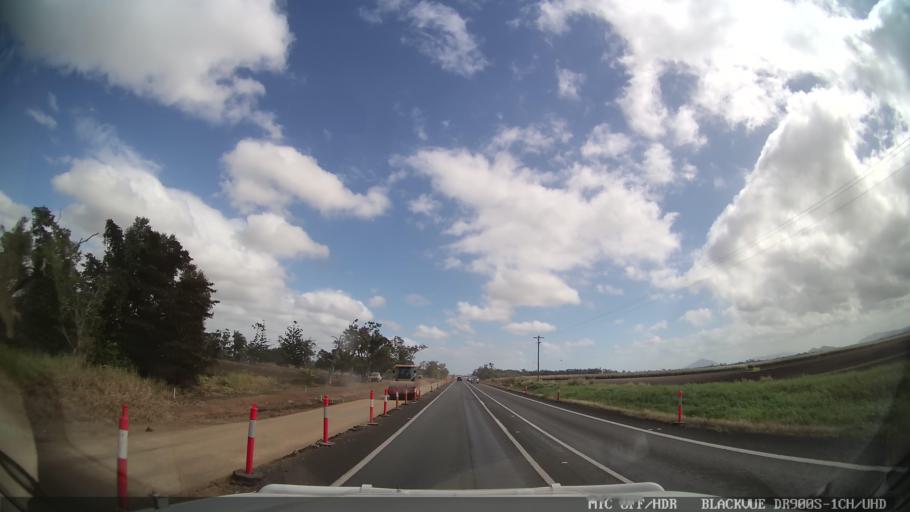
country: AU
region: Queensland
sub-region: Whitsunday
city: Red Hill
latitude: -20.2988
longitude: 148.5087
